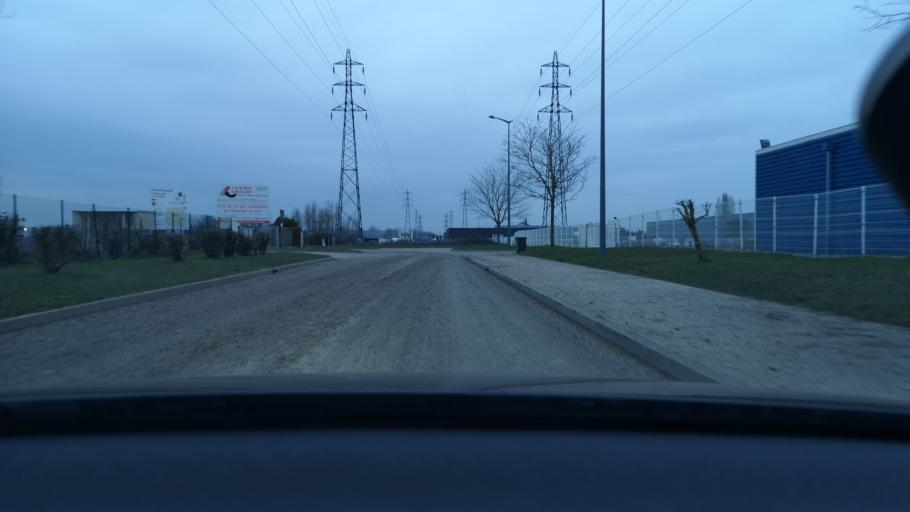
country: FR
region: Bourgogne
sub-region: Departement de Saone-et-Loire
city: Chalon-sur-Saone
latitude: 46.7652
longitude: 4.8667
